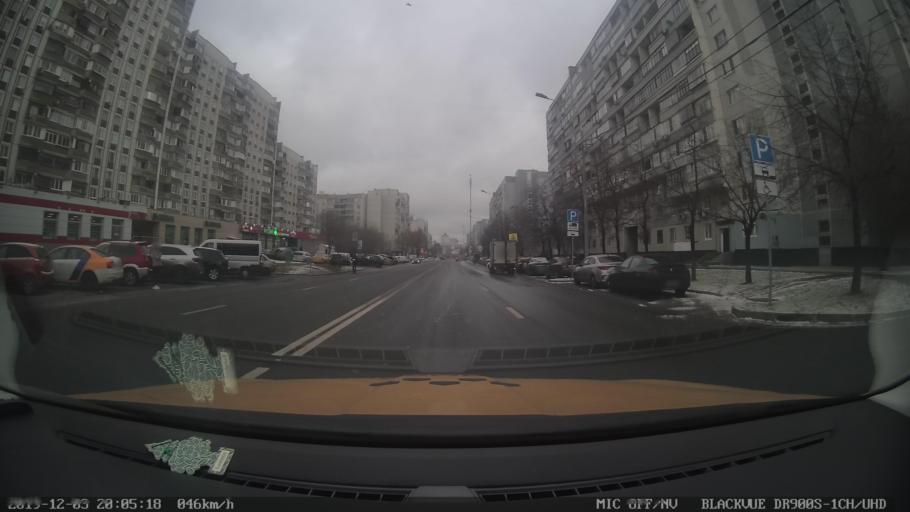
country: RU
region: Moscow
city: Brateyevo
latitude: 55.6456
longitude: 37.7538
